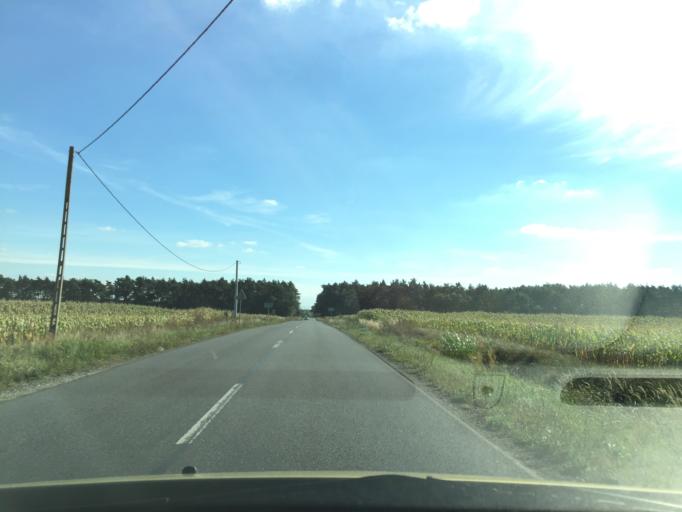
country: PL
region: Greater Poland Voivodeship
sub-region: Powiat kaliski
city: Stawiszyn
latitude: 51.9277
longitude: 18.1462
